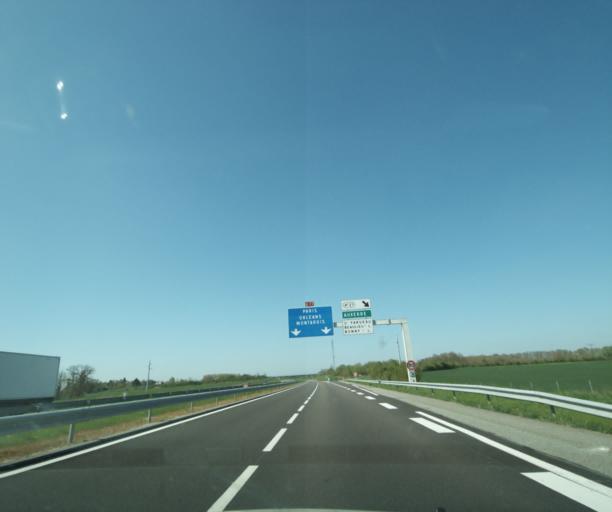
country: FR
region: Centre
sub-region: Departement du Loiret
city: Bonny-sur-Loire
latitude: 47.5674
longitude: 2.8786
